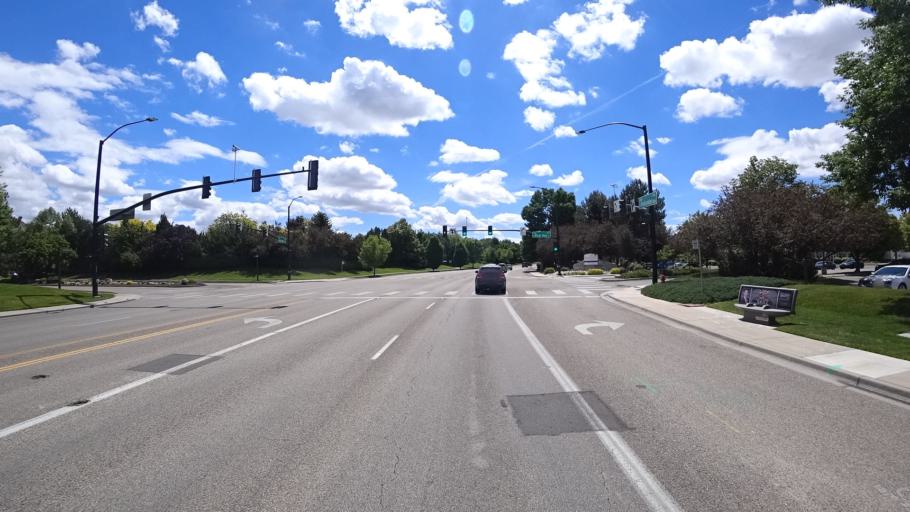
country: US
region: Idaho
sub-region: Ada County
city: Boise
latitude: 43.5896
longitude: -116.1747
